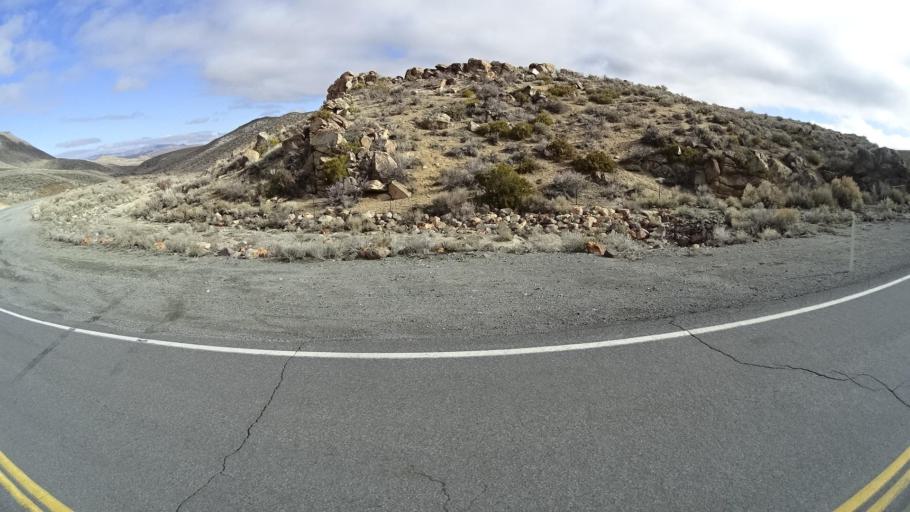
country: US
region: Nevada
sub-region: Washoe County
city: Cold Springs
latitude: 39.8034
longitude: -119.9302
